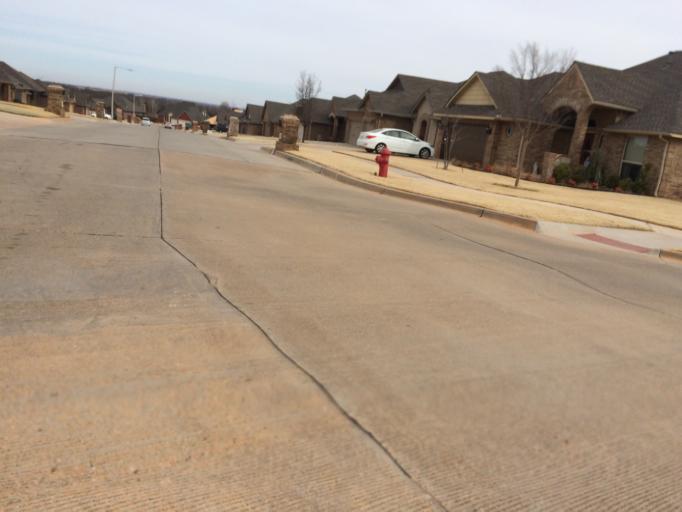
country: US
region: Oklahoma
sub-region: Cleveland County
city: Hall Park
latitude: 35.2139
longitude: -97.3889
